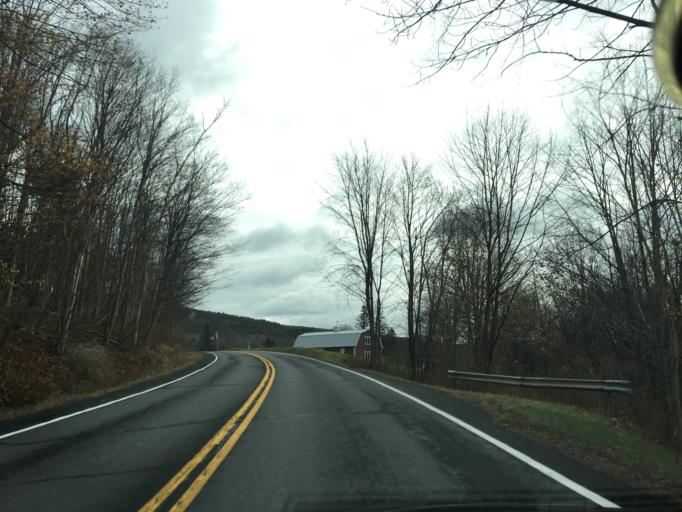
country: US
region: New York
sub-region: Rensselaer County
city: Averill Park
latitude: 42.6311
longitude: -73.5347
